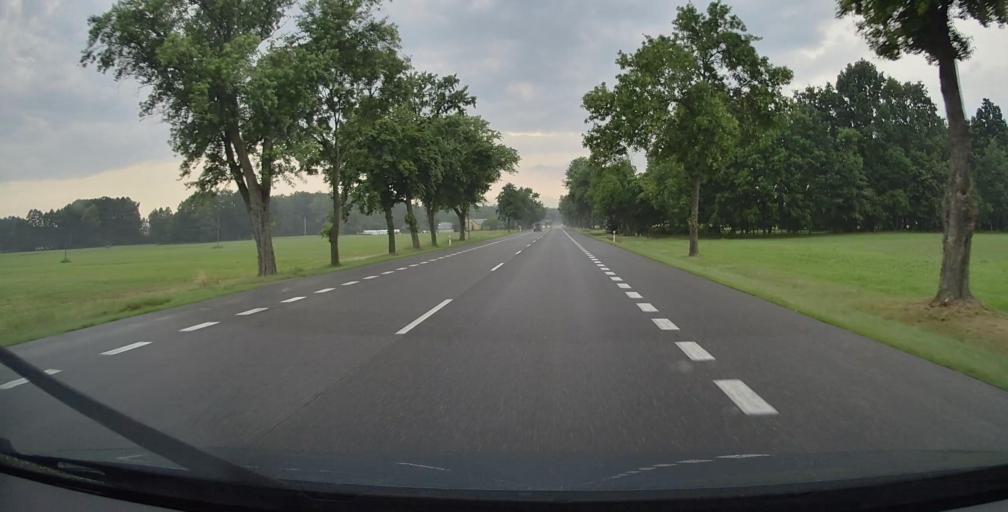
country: PL
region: Masovian Voivodeship
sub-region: Powiat siedlecki
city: Zbuczyn
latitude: 52.0744
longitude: 22.5003
